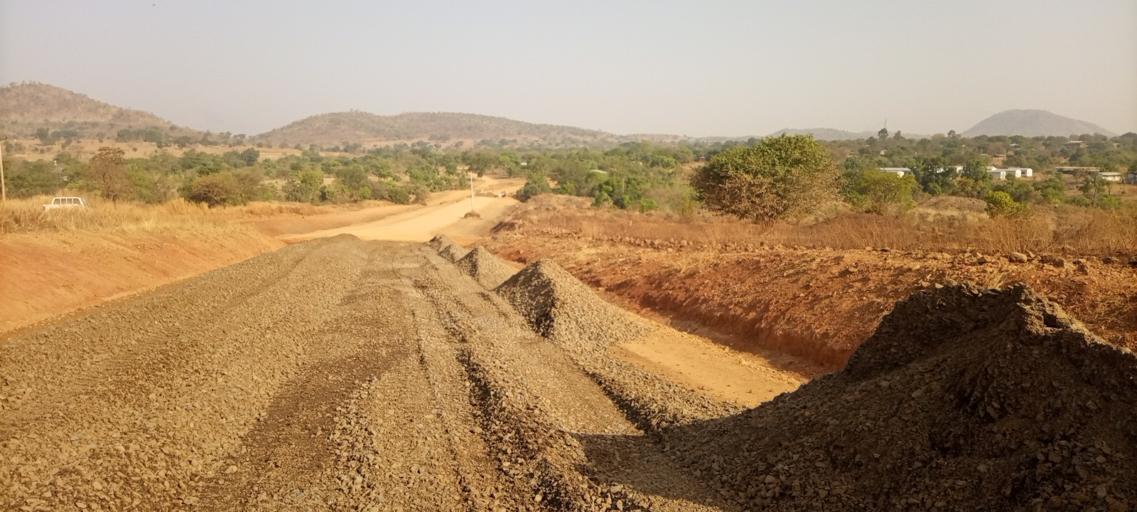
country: ET
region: Oromiya
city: Mendi
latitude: 10.2048
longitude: 35.0900
